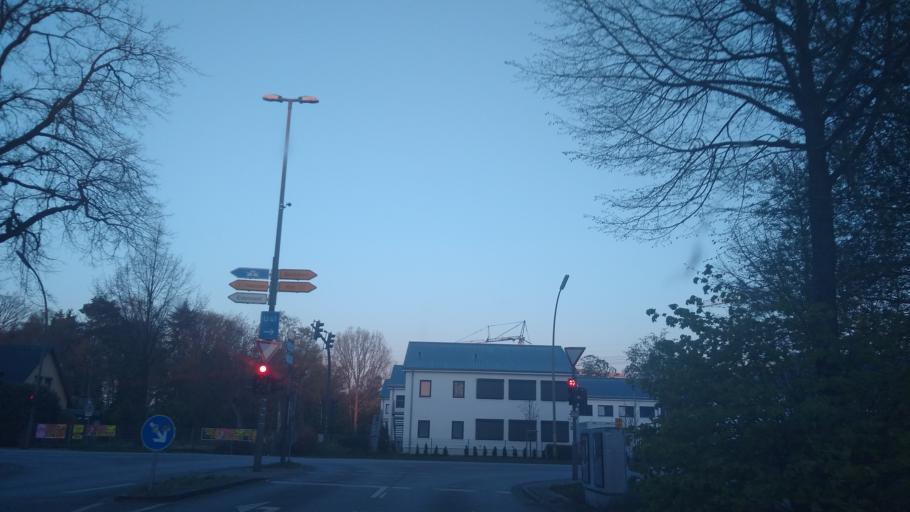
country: DE
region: Schleswig-Holstein
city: Bonningstedt
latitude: 53.6460
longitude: 9.9088
